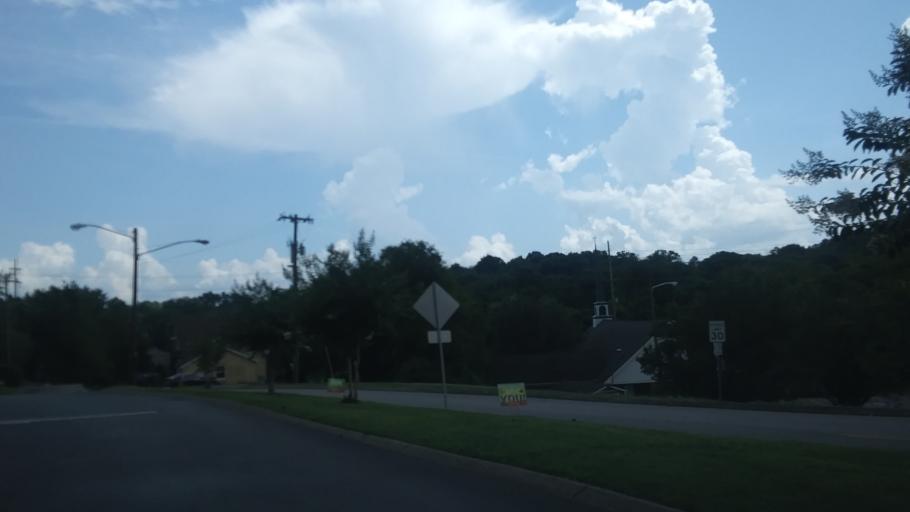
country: US
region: Tennessee
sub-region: Davidson County
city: Oak Hill
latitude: 36.0810
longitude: -86.7149
